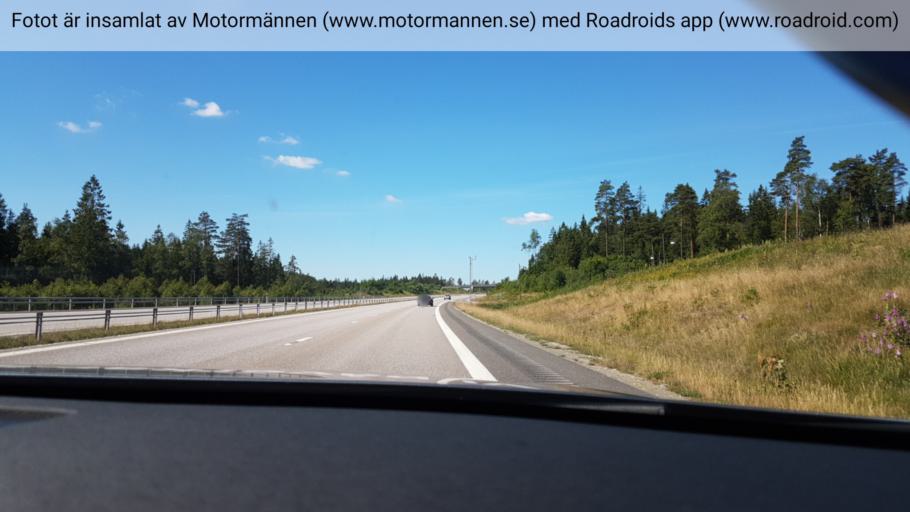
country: SE
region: Vaestra Goetaland
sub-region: Boras Kommun
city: Dalsjofors
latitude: 57.7407
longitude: 13.0502
